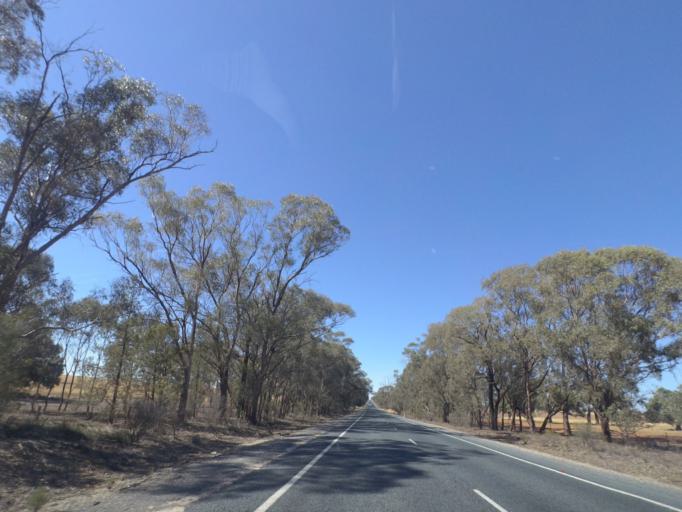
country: AU
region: New South Wales
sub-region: Bland
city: West Wyalong
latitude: -34.1480
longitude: 147.1190
